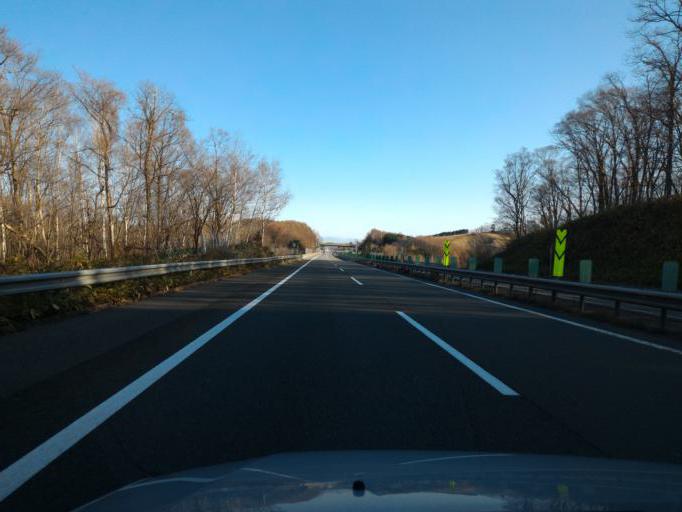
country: JP
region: Hokkaido
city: Iwamizawa
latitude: 43.1883
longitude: 141.7908
